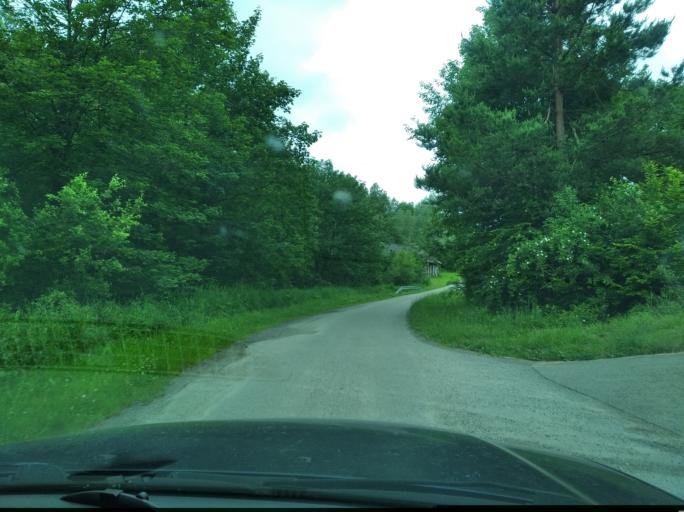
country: PL
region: Subcarpathian Voivodeship
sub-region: Powiat przemyski
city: Nienadowa
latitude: 49.8770
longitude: 22.4137
